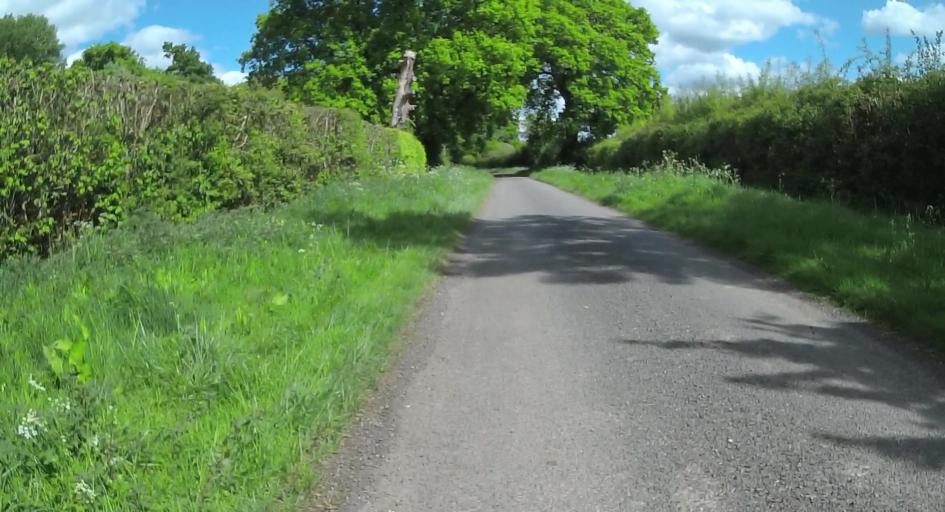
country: GB
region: England
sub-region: West Berkshire
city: Stratfield Mortimer
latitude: 51.3364
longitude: -1.0335
